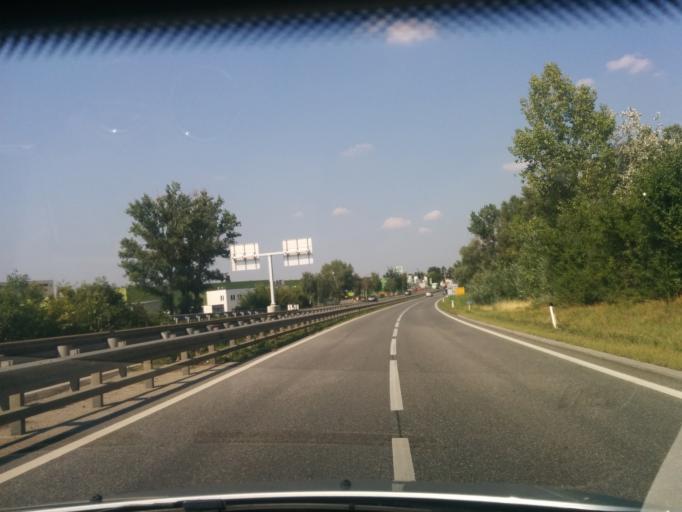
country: AT
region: Lower Austria
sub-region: Politischer Bezirk Korneuburg
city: Bisamberg
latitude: 48.3336
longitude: 16.3380
